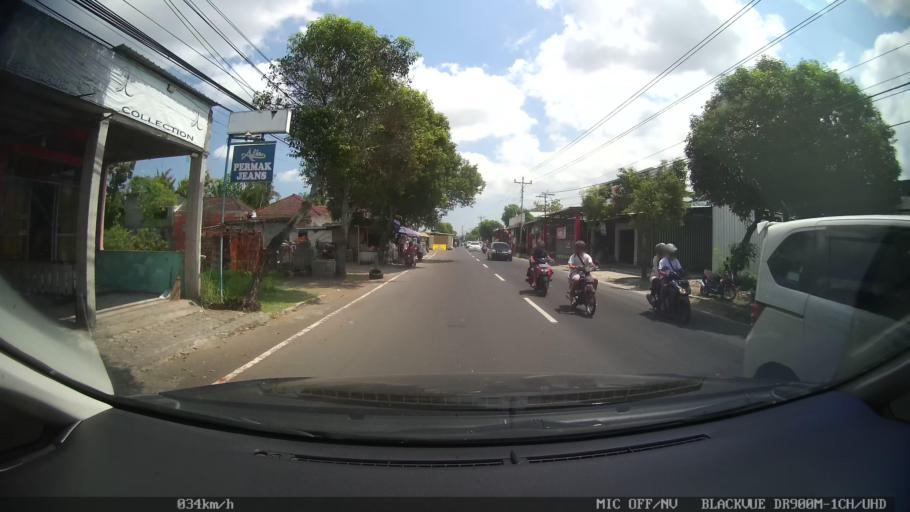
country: ID
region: Daerah Istimewa Yogyakarta
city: Bantul
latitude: -7.8945
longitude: 110.3449
